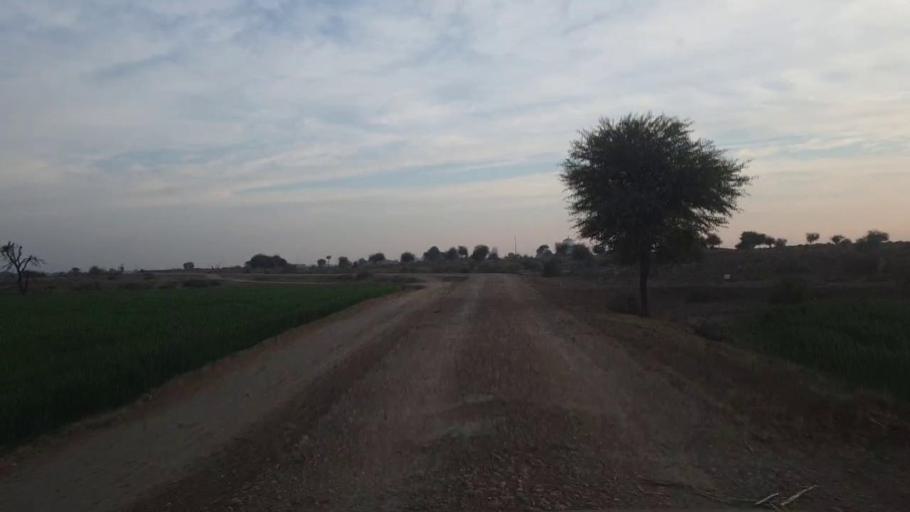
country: PK
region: Sindh
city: Shahpur Chakar
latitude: 26.0609
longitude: 68.5284
